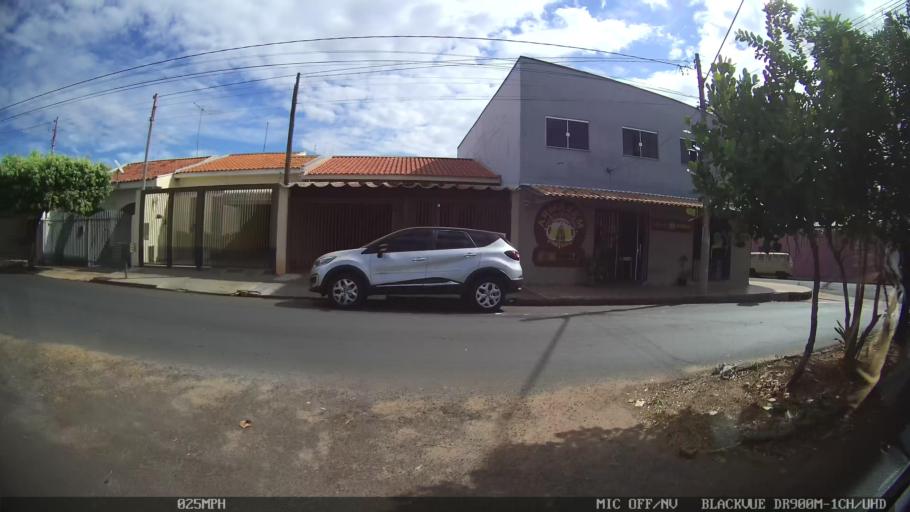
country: BR
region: Sao Paulo
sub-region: Bady Bassitt
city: Bady Bassitt
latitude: -20.8106
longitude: -49.5149
